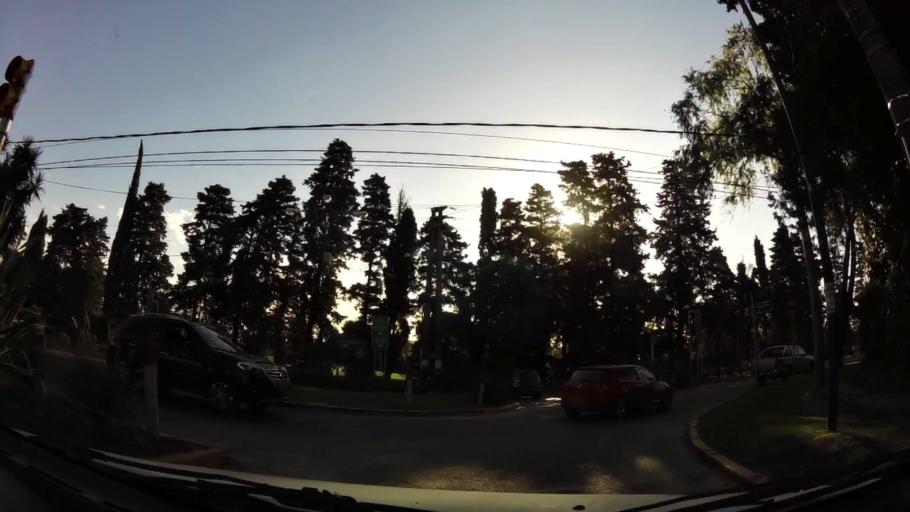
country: AR
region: Buenos Aires
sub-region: Partido de San Isidro
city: San Isidro
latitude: -34.4874
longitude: -58.5491
